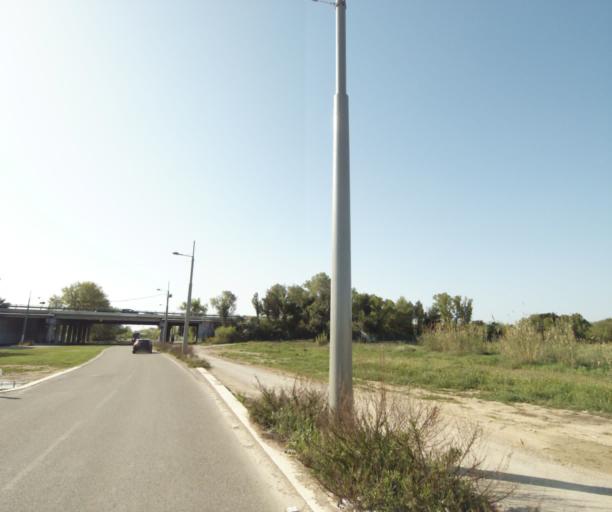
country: FR
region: Languedoc-Roussillon
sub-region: Departement de l'Herault
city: Lattes
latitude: 43.5950
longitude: 3.9052
